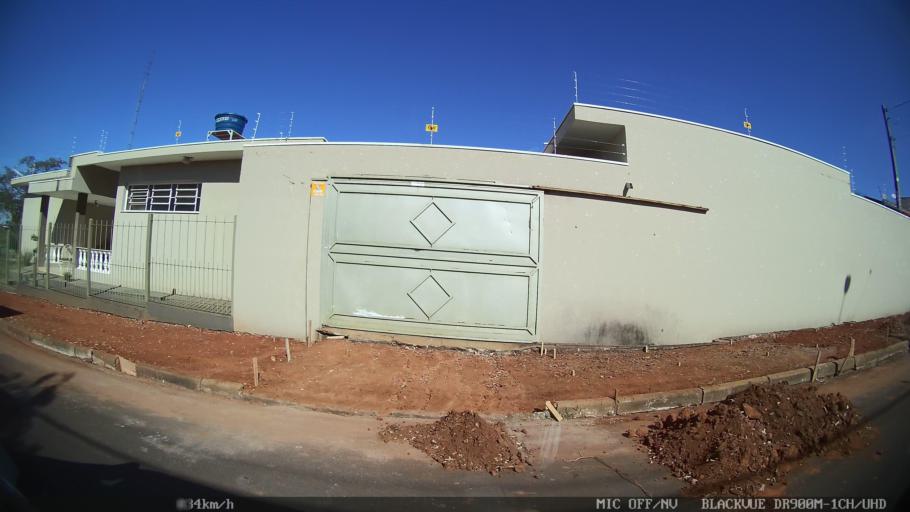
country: BR
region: Sao Paulo
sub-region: Olimpia
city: Olimpia
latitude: -20.7323
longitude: -48.9172
